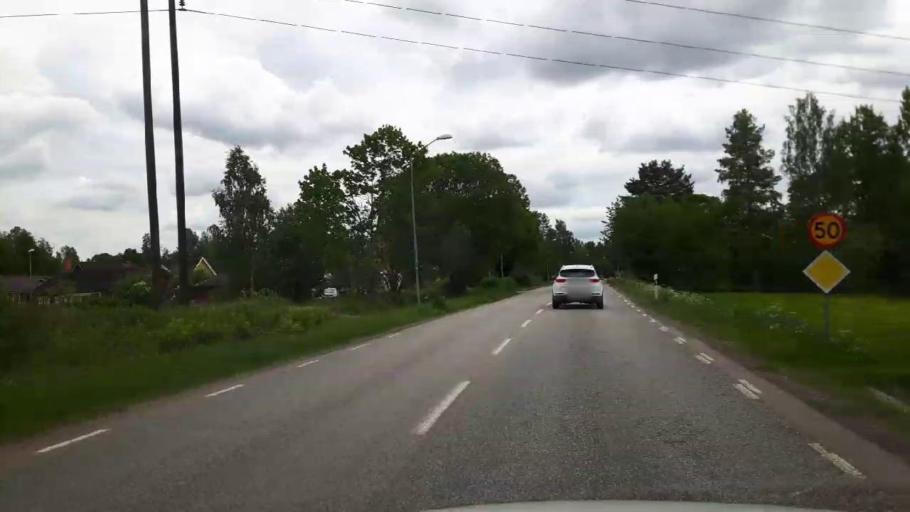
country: SE
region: Vaestmanland
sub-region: Norbergs Kommun
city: Norberg
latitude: 60.1018
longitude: 15.9274
